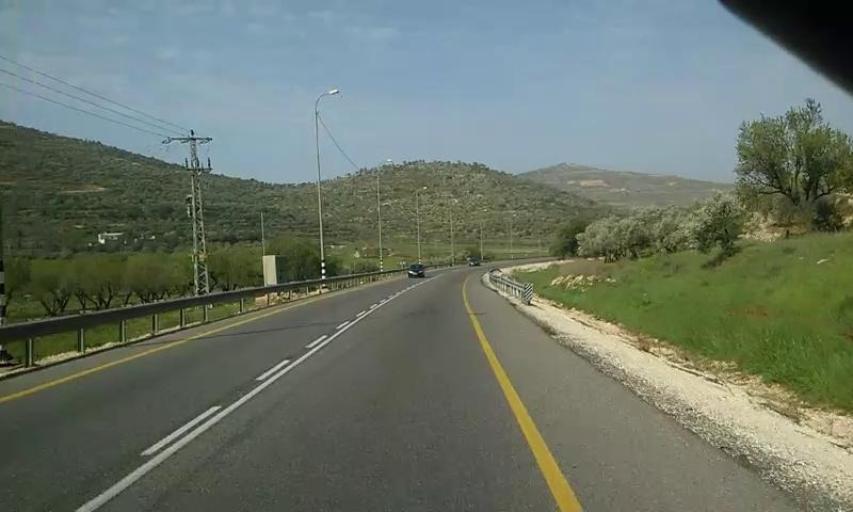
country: PS
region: West Bank
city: Al Lubban ash Sharqiyah
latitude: 32.0657
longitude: 35.2474
